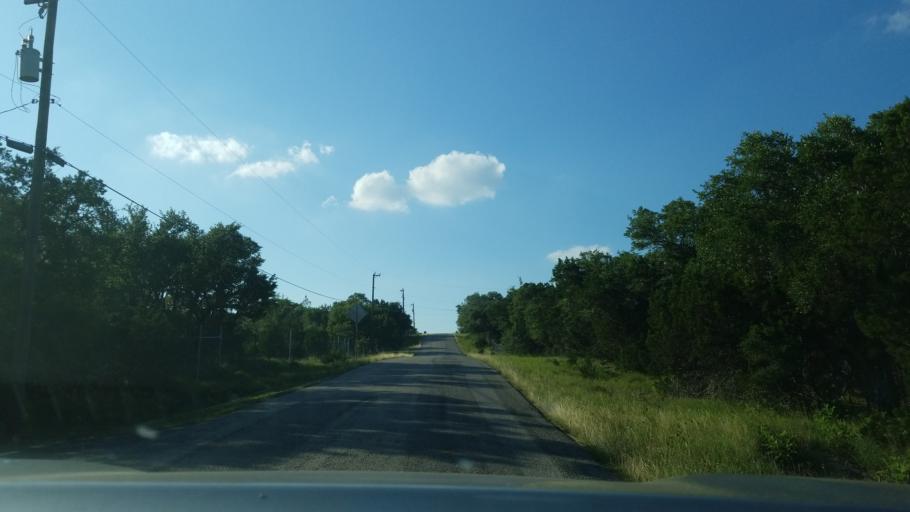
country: US
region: Texas
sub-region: Comal County
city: Bulverde
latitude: 29.7769
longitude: -98.4438
